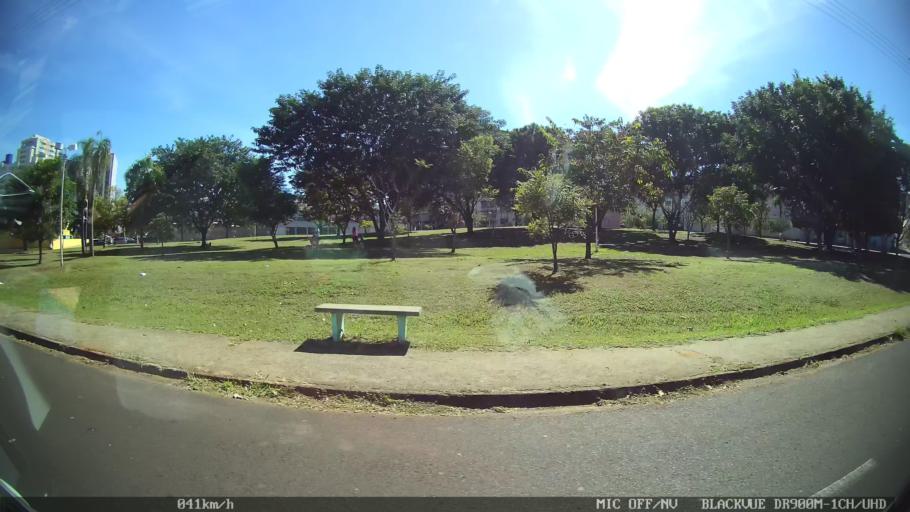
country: BR
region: Sao Paulo
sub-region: Franca
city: Franca
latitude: -20.5513
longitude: -47.4020
